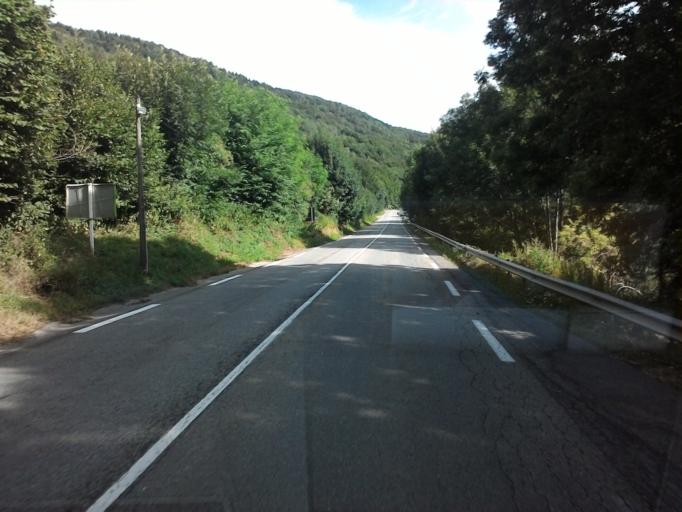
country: FR
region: Rhone-Alpes
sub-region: Departement de l'Isere
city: Pierre-Chatel
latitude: 44.9997
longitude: 5.7726
